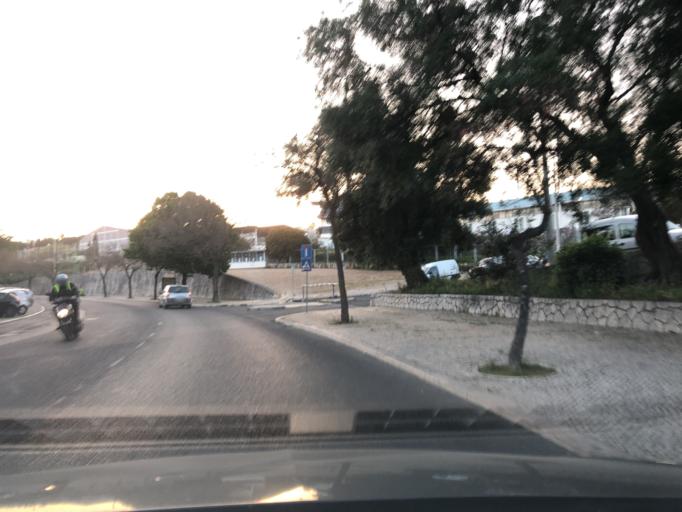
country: PT
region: Lisbon
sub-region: Oeiras
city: Alges
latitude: 38.7008
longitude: -9.2067
